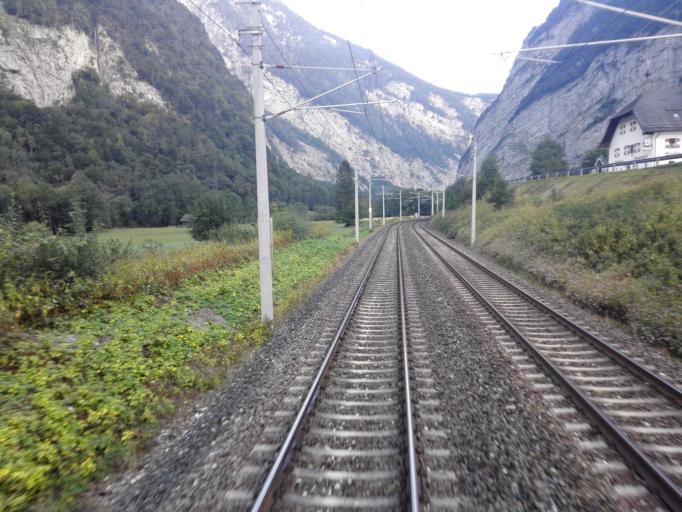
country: AT
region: Salzburg
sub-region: Politischer Bezirk Hallein
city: Golling an der Salzach
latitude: 47.5447
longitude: 13.1703
